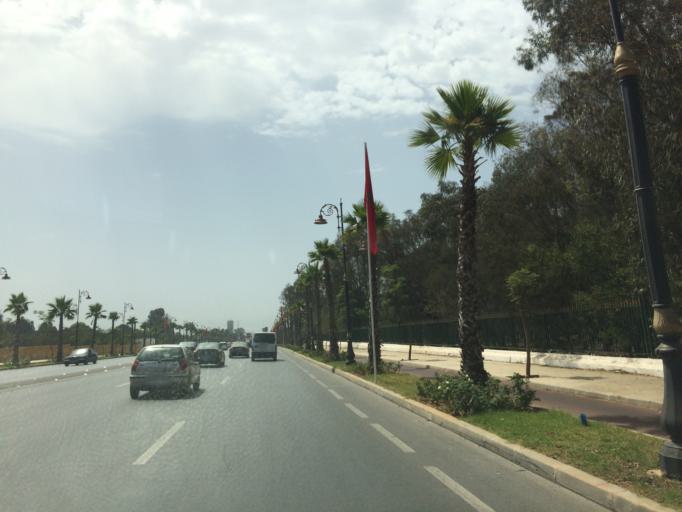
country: MA
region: Rabat-Sale-Zemmour-Zaer
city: Sale
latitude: 34.0338
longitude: -6.7816
